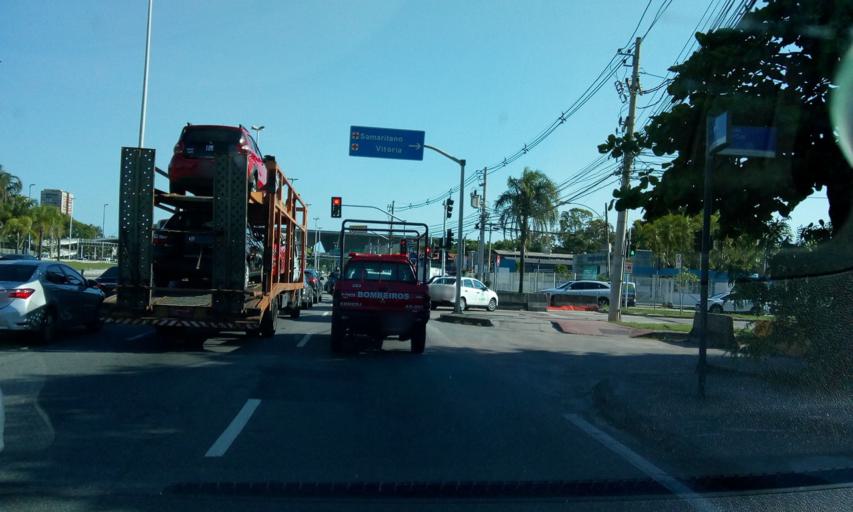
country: BR
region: Rio de Janeiro
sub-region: Rio De Janeiro
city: Rio de Janeiro
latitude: -22.9932
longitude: -43.3662
